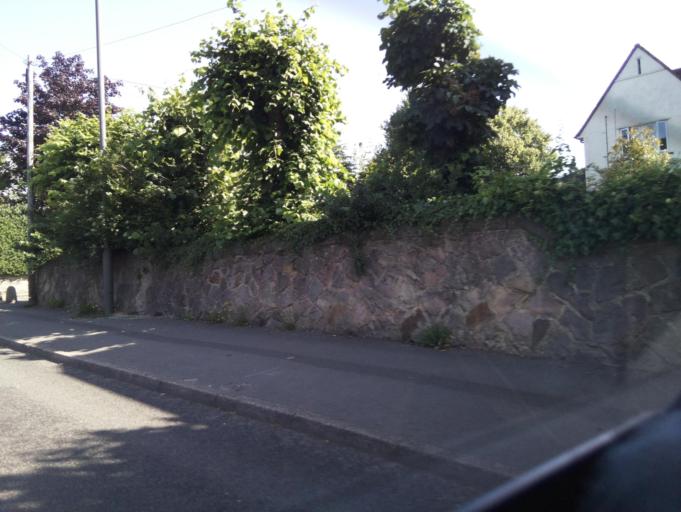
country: GB
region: England
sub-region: Derby
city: Derby
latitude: 52.9086
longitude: -1.5018
